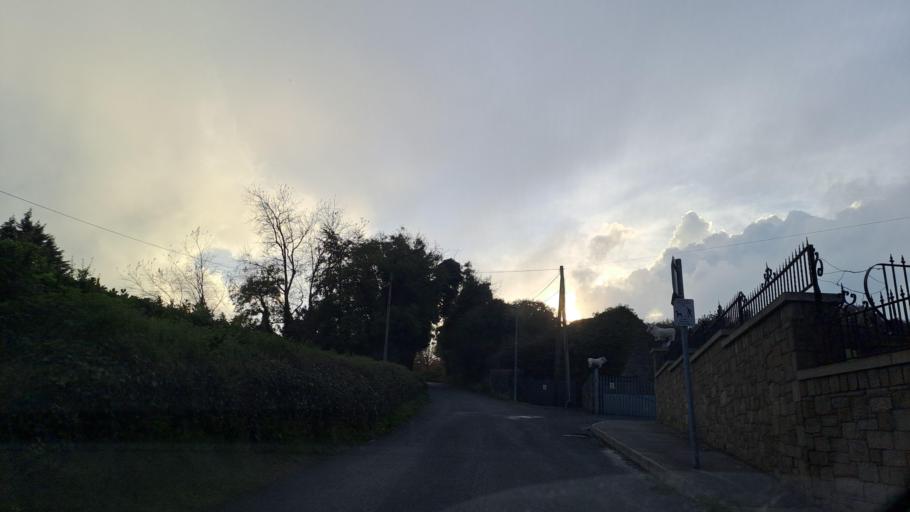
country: IE
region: Ulster
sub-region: County Monaghan
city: Carrickmacross
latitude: 53.9769
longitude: -6.7269
